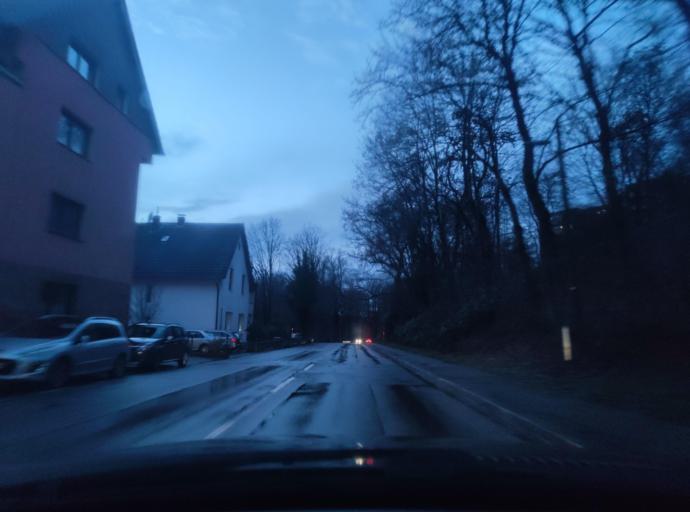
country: DE
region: North Rhine-Westphalia
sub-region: Regierungsbezirk Dusseldorf
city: Essen
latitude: 51.4242
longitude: 7.0722
